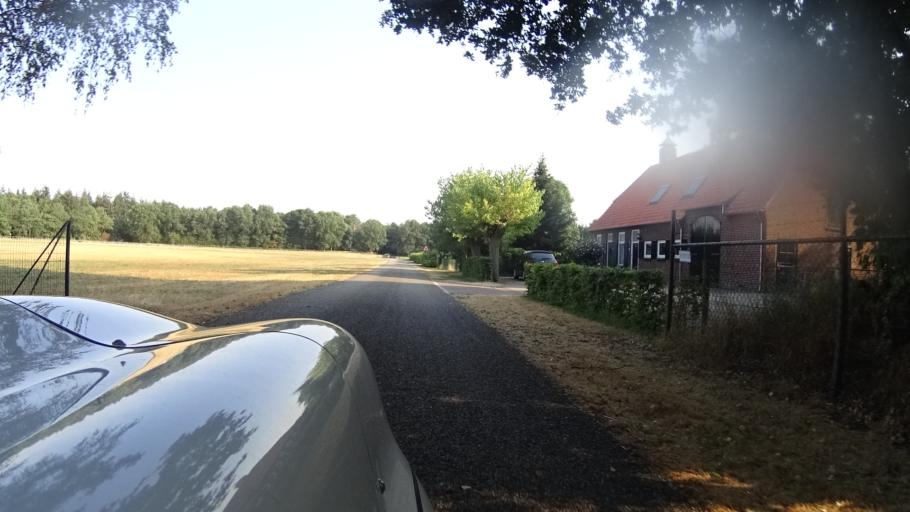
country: NL
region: North Brabant
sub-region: Gemeente Mill en Sint Hubert
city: Wilbertoord
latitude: 51.6845
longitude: 5.7549
